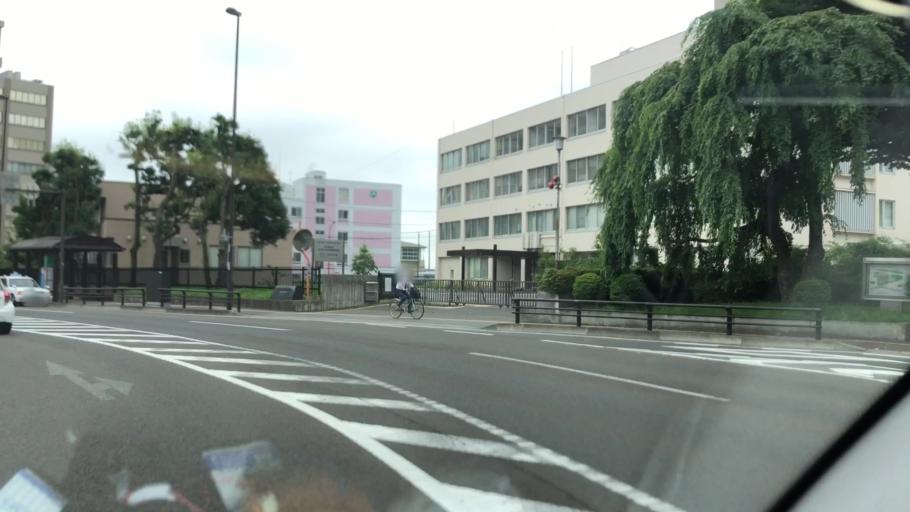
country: JP
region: Miyagi
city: Sendai-shi
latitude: 38.2629
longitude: 140.8980
